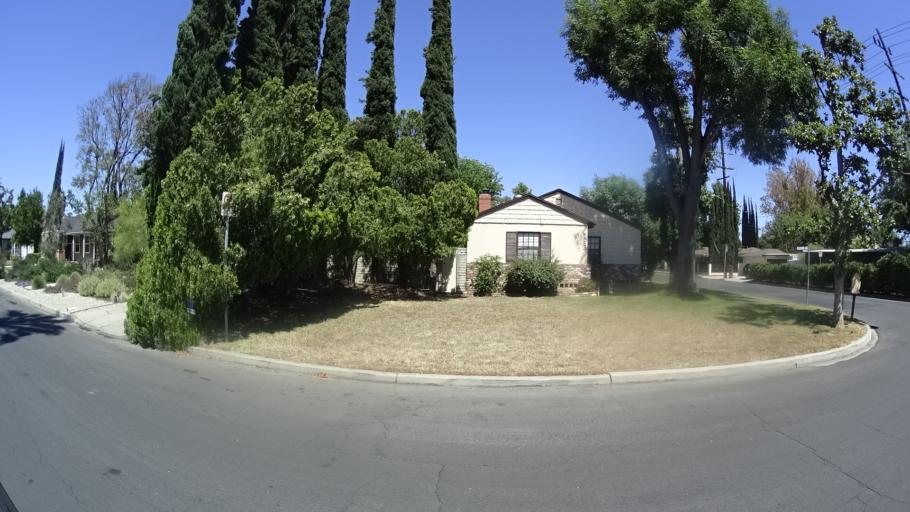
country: US
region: California
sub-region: Los Angeles County
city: Van Nuys
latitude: 34.1894
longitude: -118.4728
